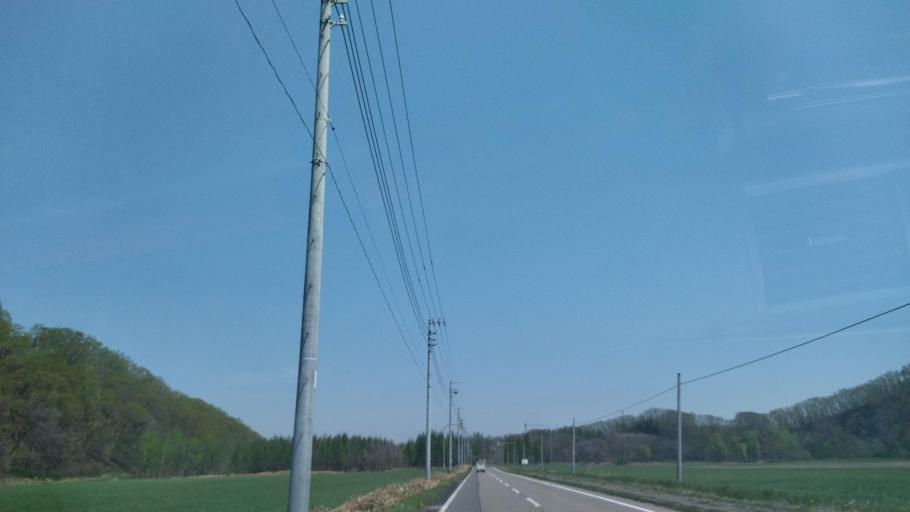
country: JP
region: Hokkaido
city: Obihiro
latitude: 42.8214
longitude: 142.9847
